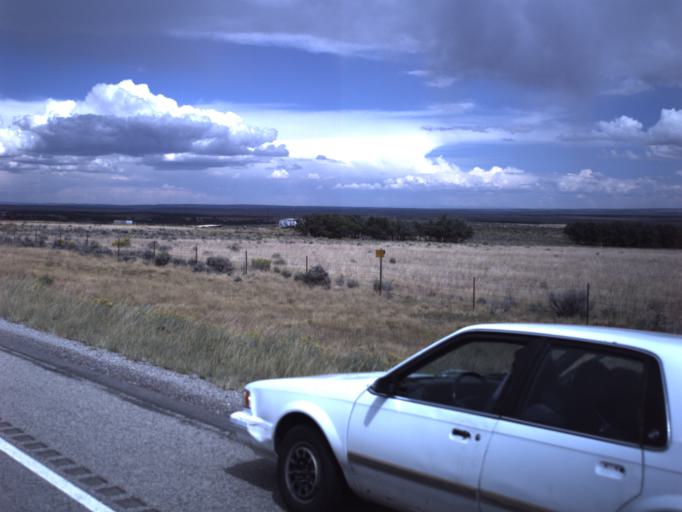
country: US
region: Utah
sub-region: San Juan County
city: Monticello
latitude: 37.8459
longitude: -109.3369
